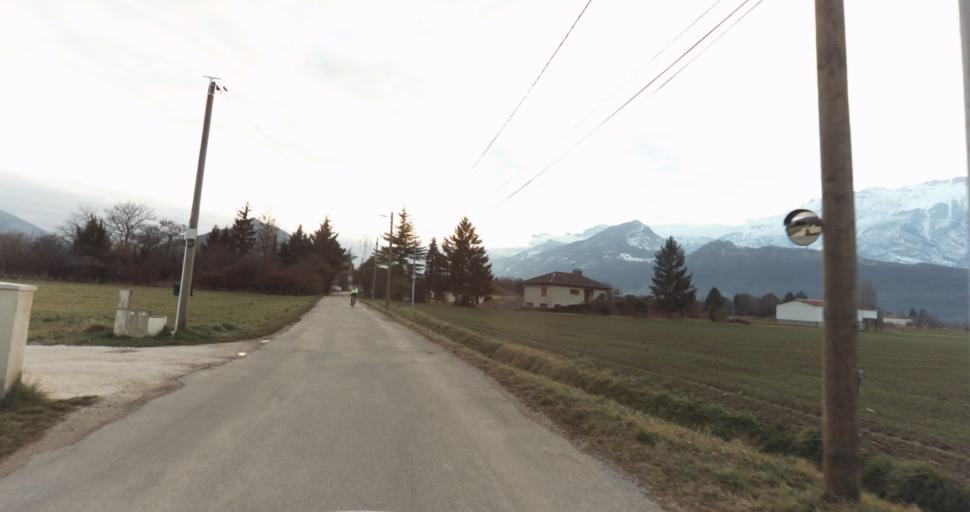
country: FR
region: Rhone-Alpes
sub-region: Departement de l'Isere
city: Vif
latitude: 45.0746
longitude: 5.6995
